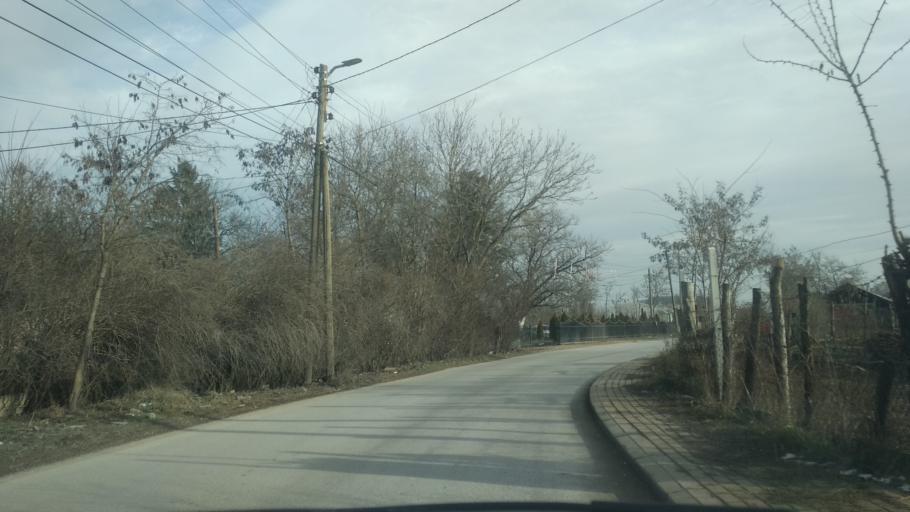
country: XK
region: Pristina
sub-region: Kosovo Polje
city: Kosovo Polje
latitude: 42.5957
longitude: 21.1249
